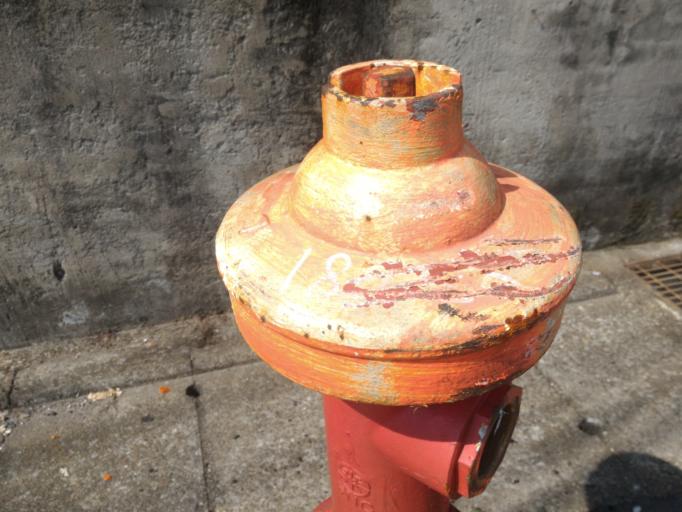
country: TW
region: Taipei
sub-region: Taipei
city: Banqiao
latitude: 24.9620
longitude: 121.4007
